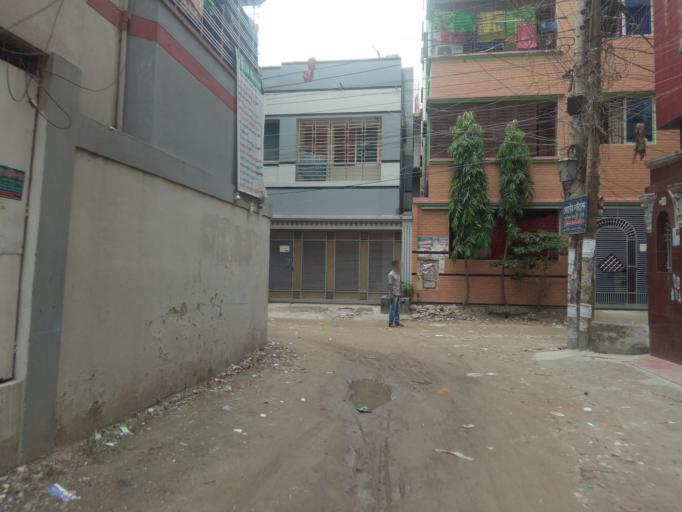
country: BD
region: Dhaka
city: Paltan
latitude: 23.7545
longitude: 90.4414
